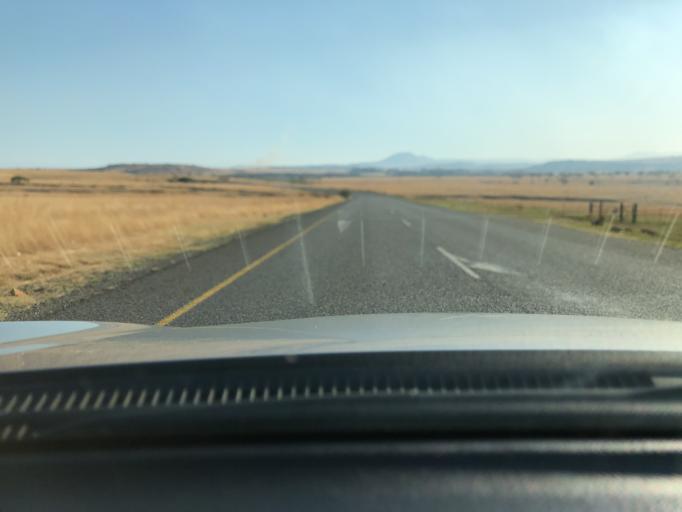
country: ZA
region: KwaZulu-Natal
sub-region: uThukela District Municipality
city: Ekuvukeni
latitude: -28.3496
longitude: 30.0276
